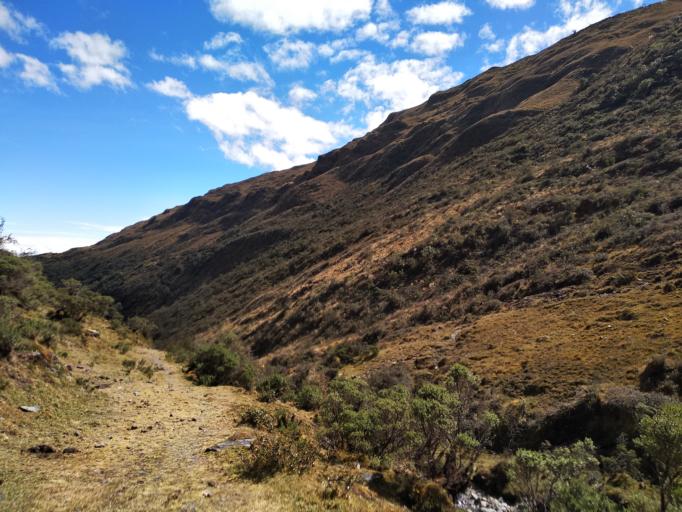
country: PE
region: Cusco
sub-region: Provincia de Urubamba
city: Ollantaytambo
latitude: -13.1373
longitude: -72.3181
